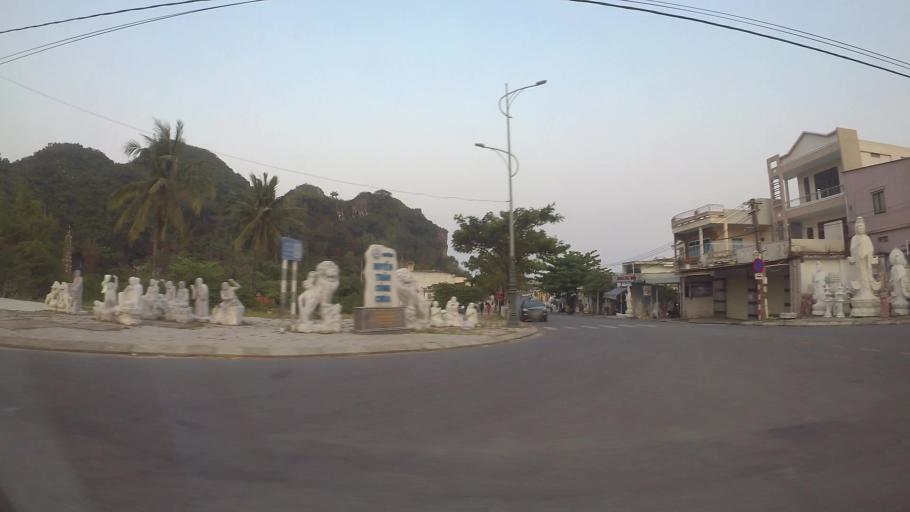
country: VN
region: Da Nang
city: Ngu Hanh Son
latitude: 16.0028
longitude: 108.2598
